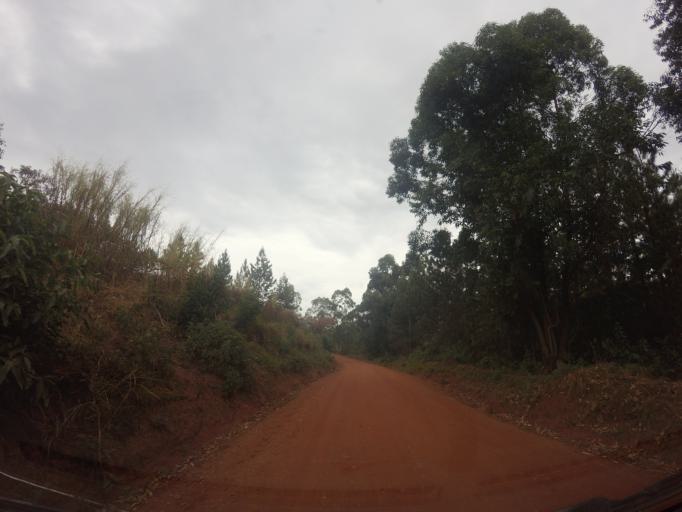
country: UG
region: Northern Region
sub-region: Zombo District
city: Zombo
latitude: 2.7655
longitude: 30.8571
